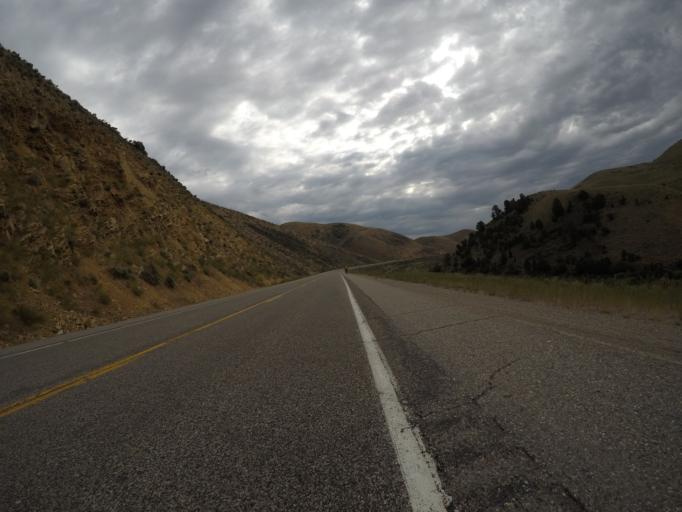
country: US
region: Wyoming
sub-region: Lincoln County
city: Kemmerer
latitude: 41.8241
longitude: -110.8553
